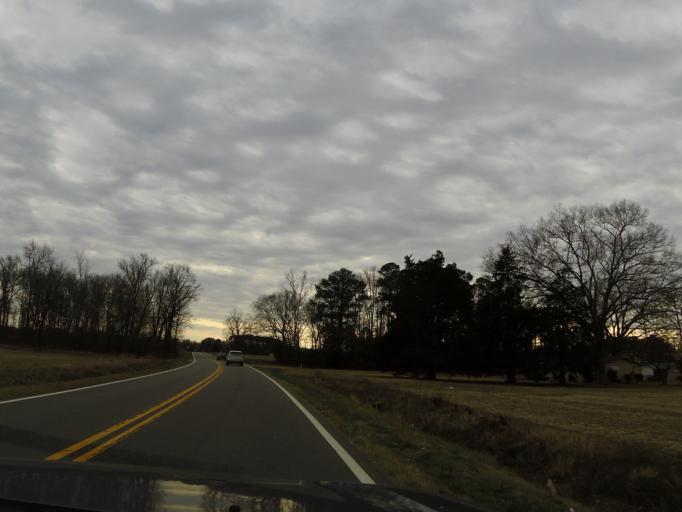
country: US
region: North Carolina
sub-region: Halifax County
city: Scotland Neck
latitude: 36.0245
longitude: -77.5006
